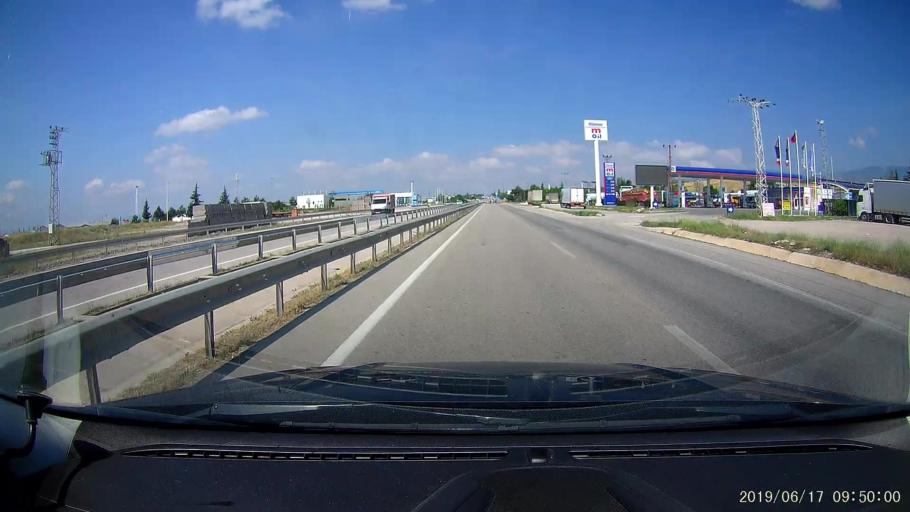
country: TR
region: Amasya
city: Merzifon
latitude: 40.8718
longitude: 35.5171
